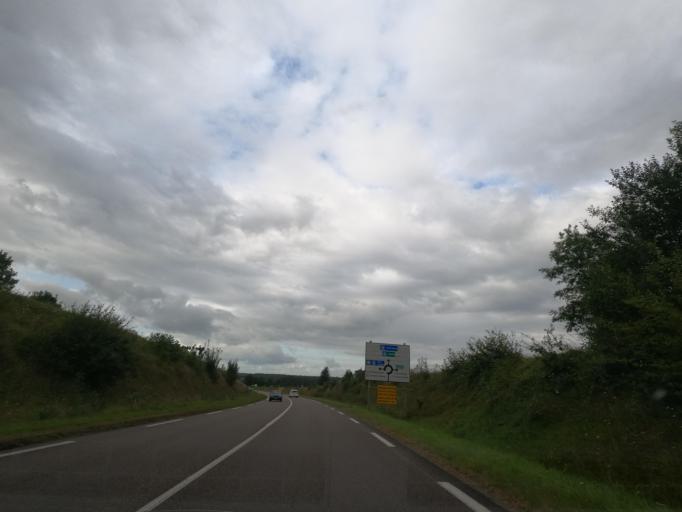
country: FR
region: Haute-Normandie
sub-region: Departement de l'Eure
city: Bourgtheroulde-Infreville
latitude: 49.2958
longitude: 0.8832
